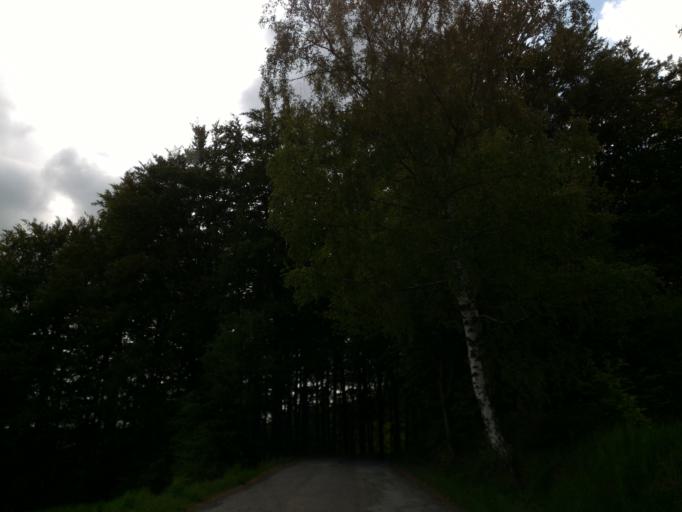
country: CZ
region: Vysocina
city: Ledec nad Sazavou
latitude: 49.6210
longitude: 15.3189
